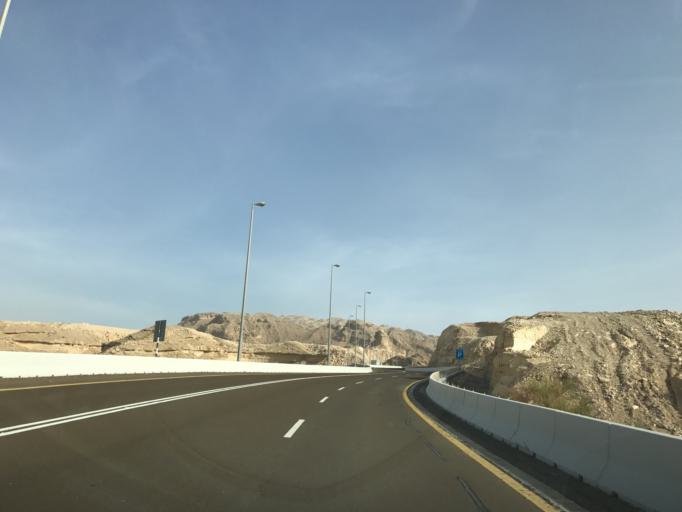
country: AE
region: Abu Dhabi
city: Al Ain
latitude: 24.1097
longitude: 55.7571
